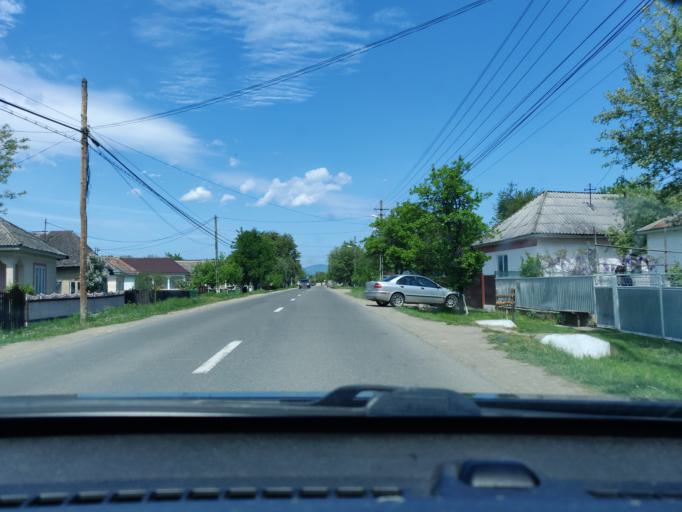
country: RO
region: Vrancea
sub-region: Comuna Campuri
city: Campuri
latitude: 46.0131
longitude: 26.7906
